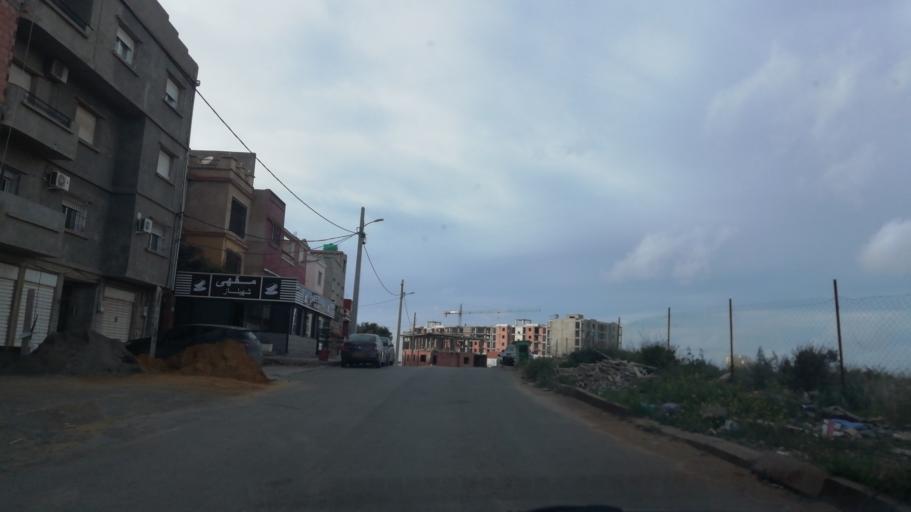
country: DZ
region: Oran
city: Bir el Djir
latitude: 35.7309
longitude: -0.5687
